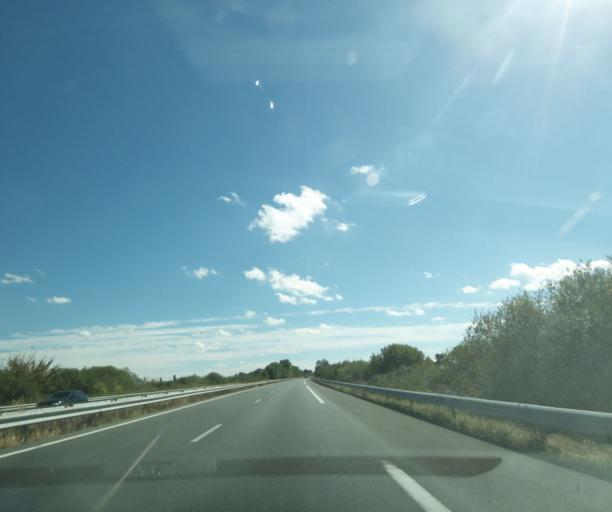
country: FR
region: Aquitaine
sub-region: Departement du Lot-et-Garonne
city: Tonneins
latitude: 44.3687
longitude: 0.2405
